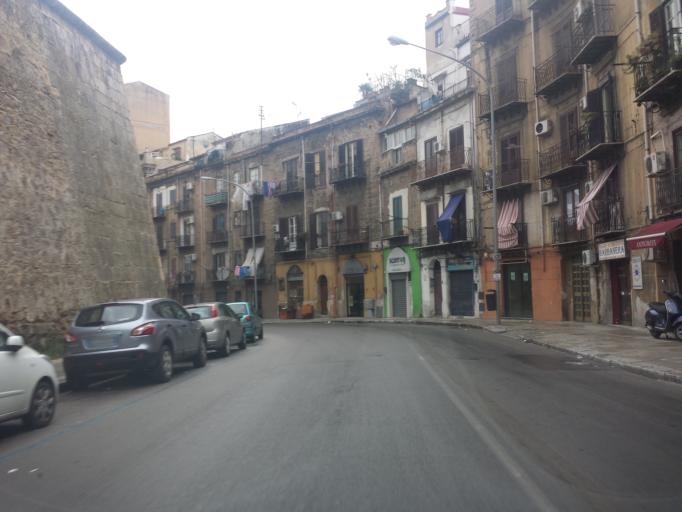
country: IT
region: Sicily
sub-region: Palermo
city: Palermo
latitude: 38.1169
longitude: 13.3507
